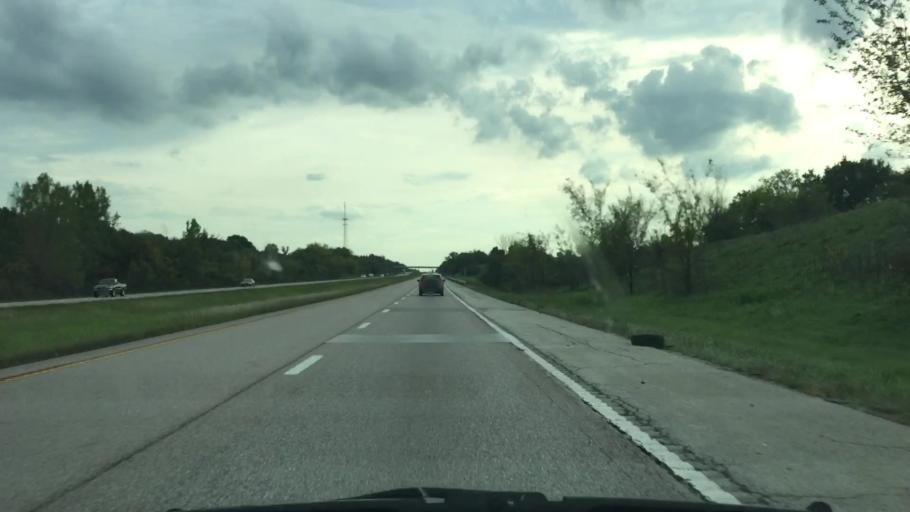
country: US
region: Missouri
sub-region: Clinton County
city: Lathrop
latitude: 39.5070
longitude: -94.2913
